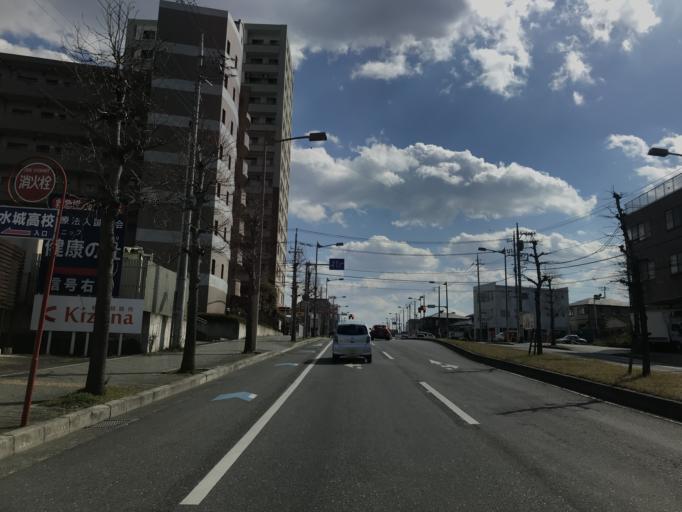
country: JP
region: Ibaraki
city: Mito-shi
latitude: 36.3615
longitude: 140.4746
